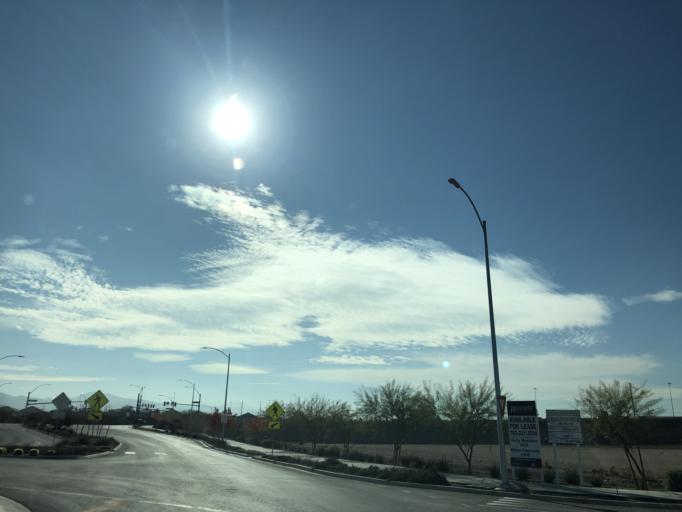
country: US
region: Nevada
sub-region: Clark County
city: Whitney
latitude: 36.0733
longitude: -115.0330
